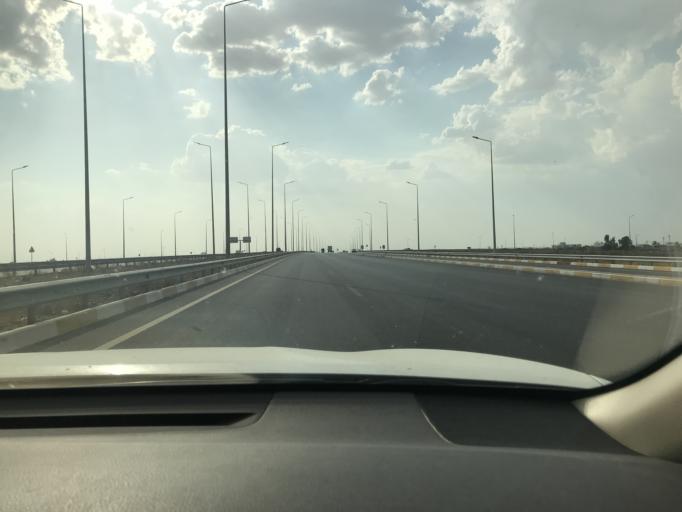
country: IQ
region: Arbil
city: Erbil
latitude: 36.1400
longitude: 43.9833
